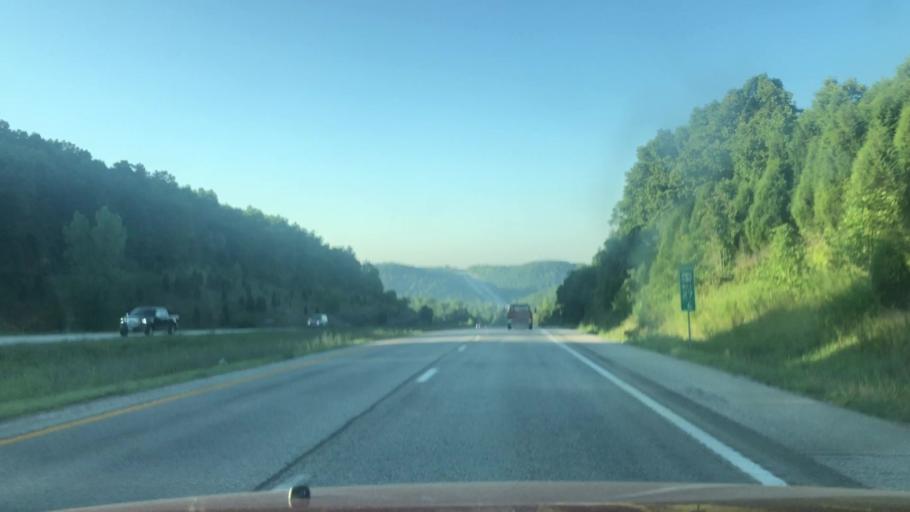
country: US
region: Missouri
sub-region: Christian County
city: Ozark
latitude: 36.8738
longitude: -93.2312
